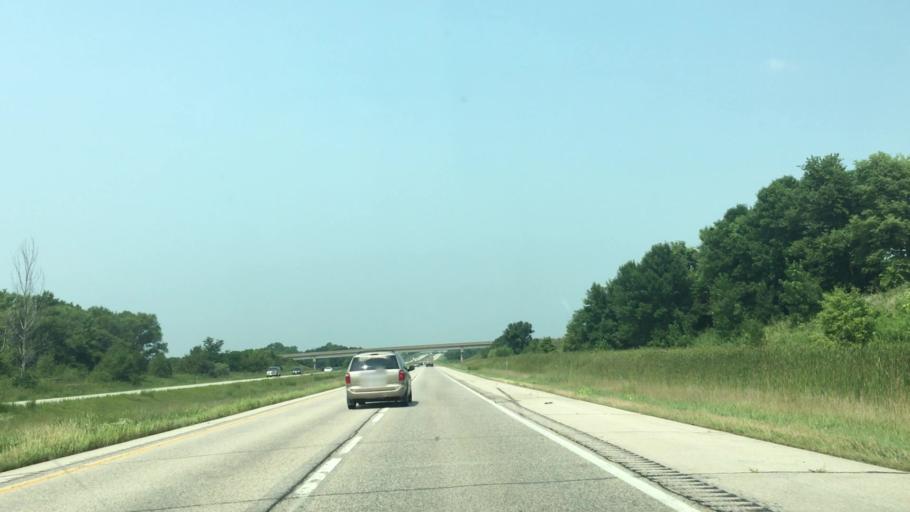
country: US
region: Iowa
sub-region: Linn County
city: Center Point
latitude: 42.1380
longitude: -91.7356
